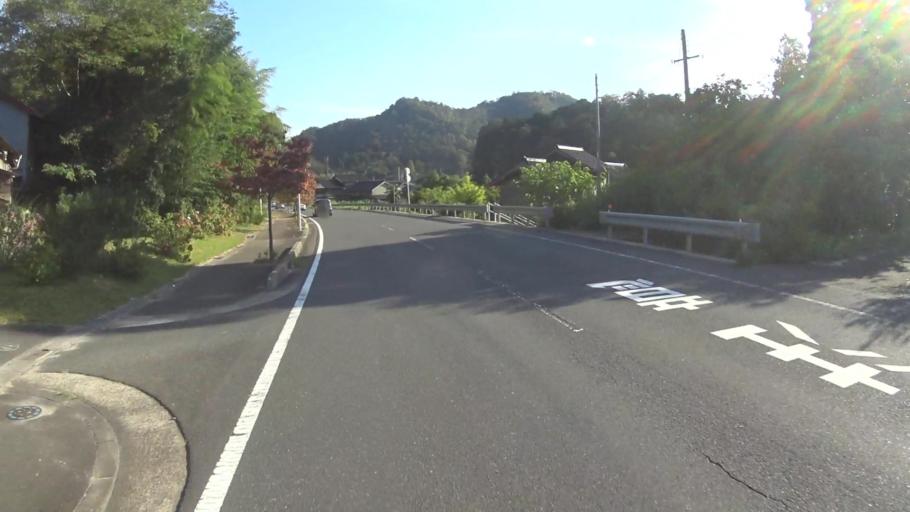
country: JP
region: Hyogo
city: Toyooka
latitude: 35.6121
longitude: 134.9190
